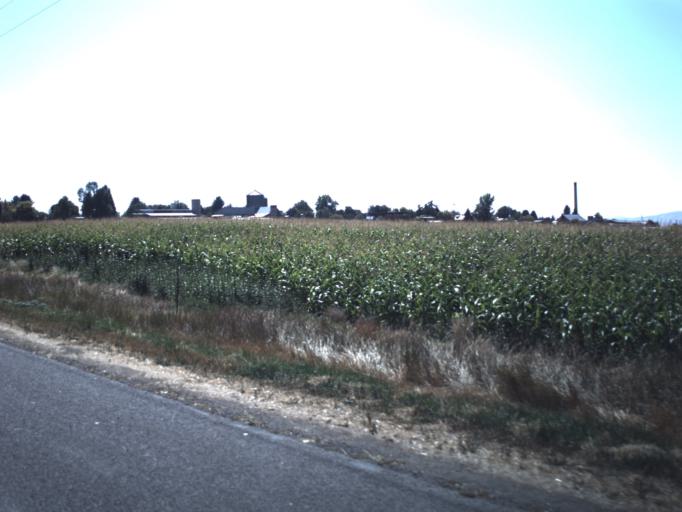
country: US
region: Utah
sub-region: Cache County
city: Richmond
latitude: 41.9271
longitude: -111.8143
